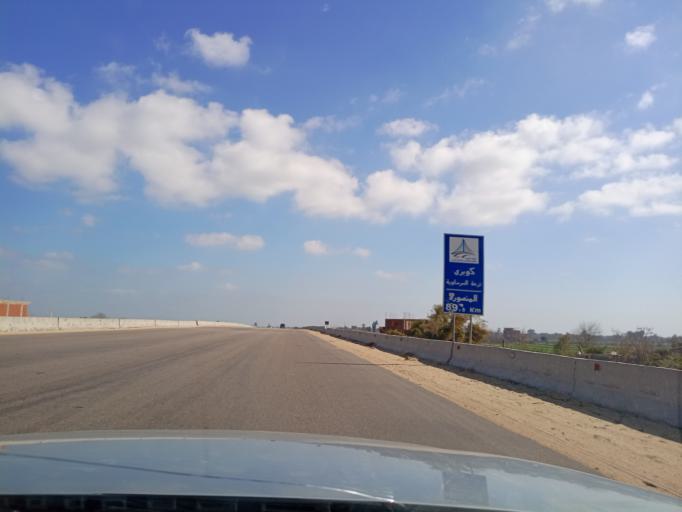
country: EG
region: Muhafazat al Minufiyah
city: Al Bajur
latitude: 30.3967
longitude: 31.0126
